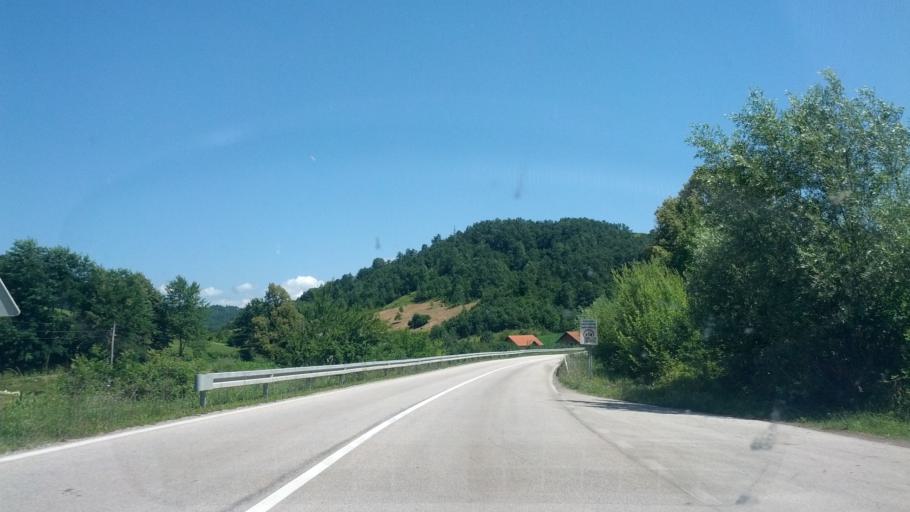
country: BA
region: Federation of Bosnia and Herzegovina
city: Bosanska Krupa
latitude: 44.9231
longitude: 16.1463
